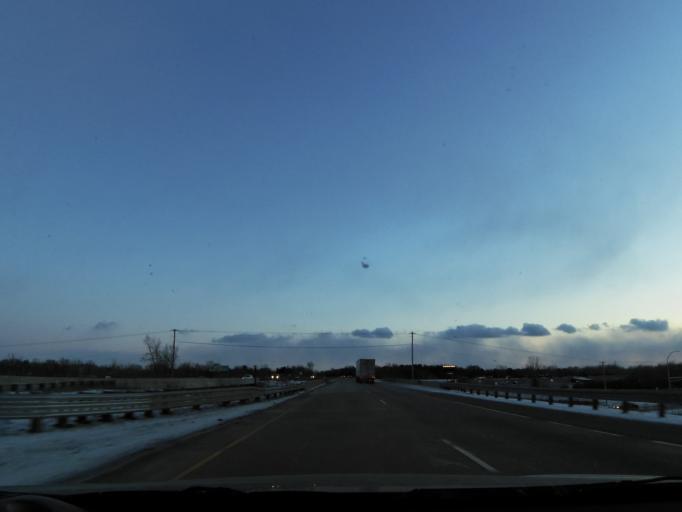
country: US
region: Minnesota
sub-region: Ramsey County
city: North Saint Paul
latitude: 44.9984
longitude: -92.9593
